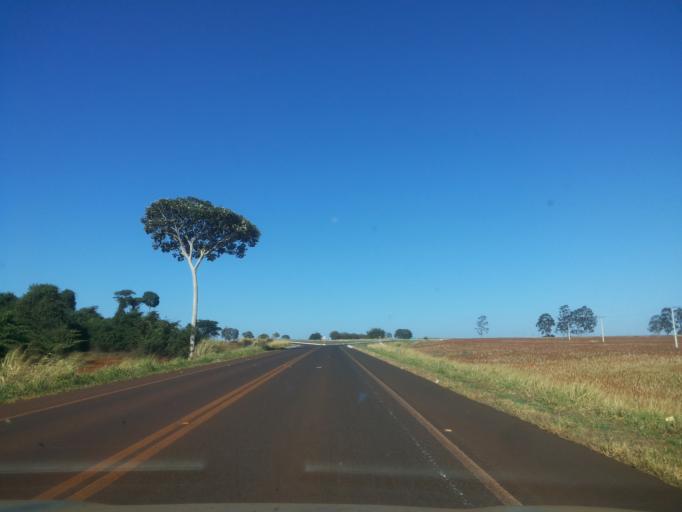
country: BR
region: Minas Gerais
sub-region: Centralina
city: Centralina
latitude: -18.7445
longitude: -49.2074
